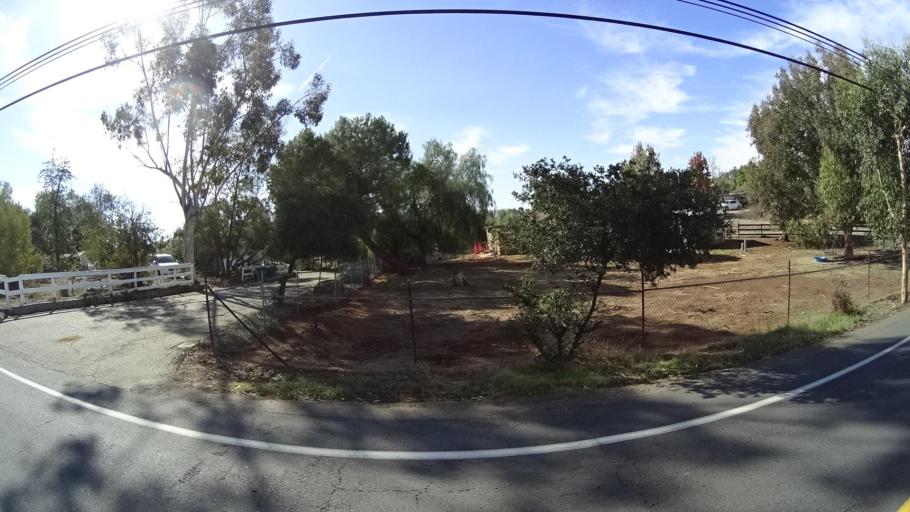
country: US
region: California
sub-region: San Diego County
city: Harbison Canyon
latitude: 32.8190
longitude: -116.8001
